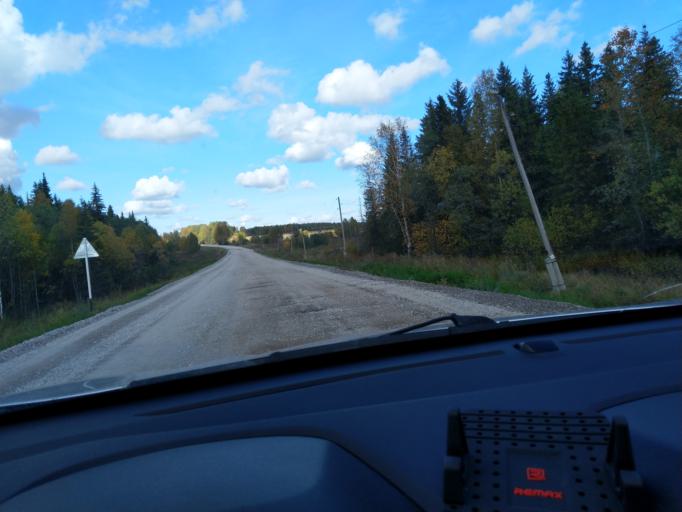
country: RU
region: Perm
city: Usol'ye
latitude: 59.4652
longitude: 56.3702
